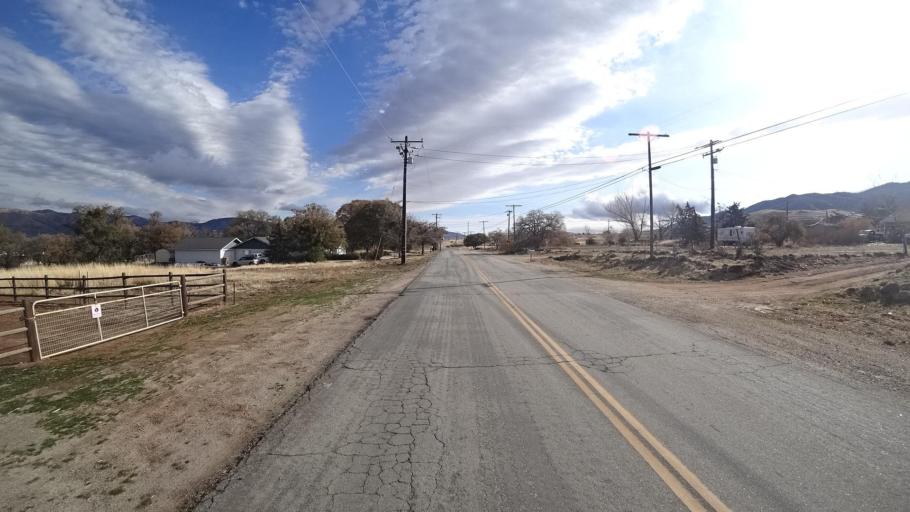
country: US
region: California
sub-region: Kern County
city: Golden Hills
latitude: 35.1169
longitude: -118.4972
